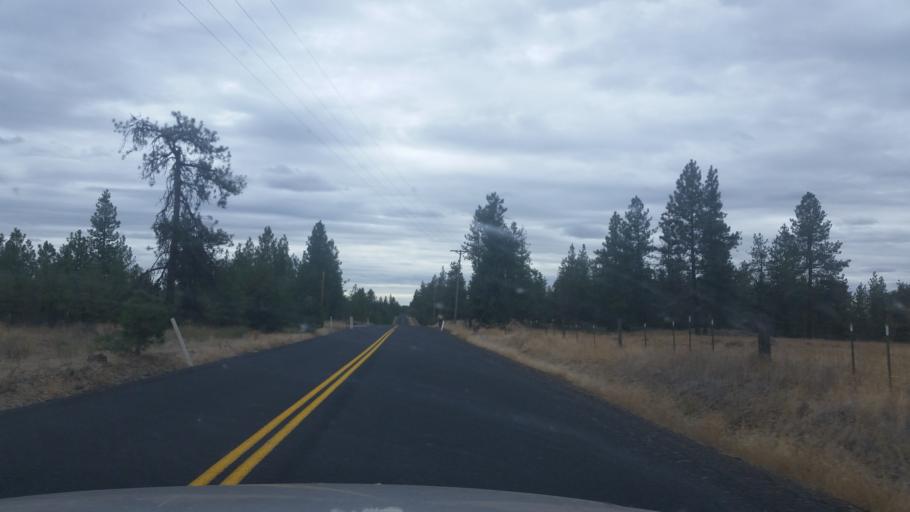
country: US
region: Washington
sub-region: Spokane County
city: Medical Lake
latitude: 47.4649
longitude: -117.7792
